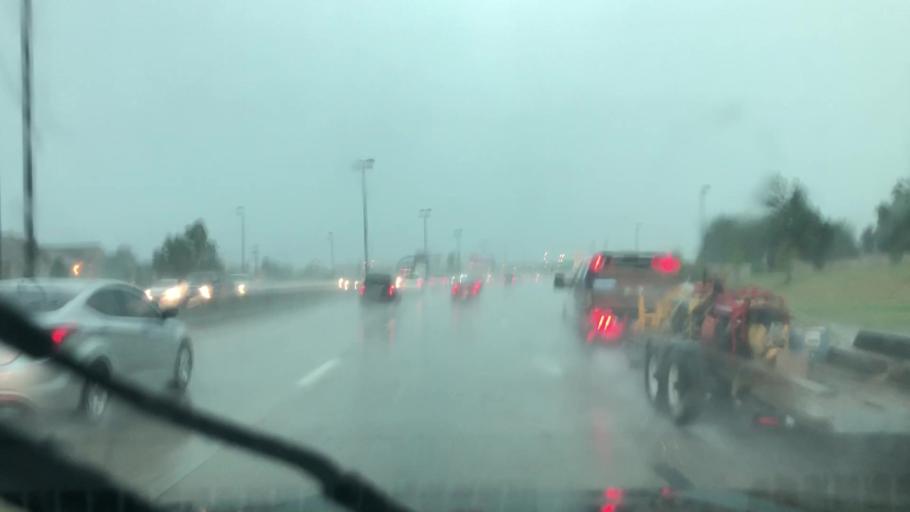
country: US
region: Oklahoma
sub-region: Tulsa County
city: Jenks
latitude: 36.0919
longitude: -95.9292
